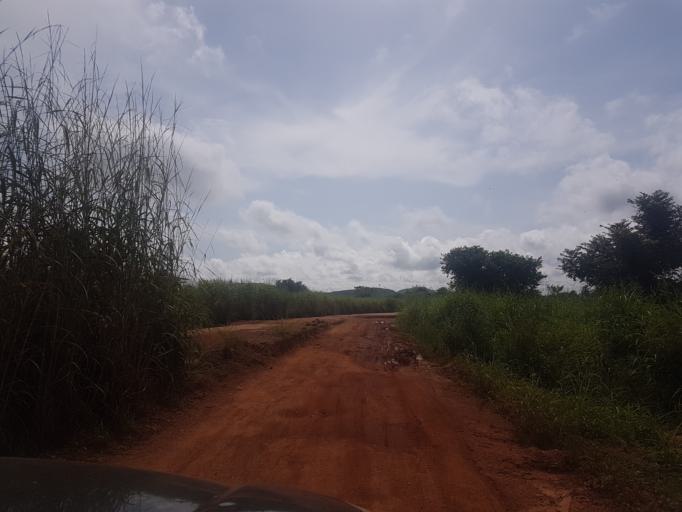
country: GN
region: Nzerekore
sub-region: Prefecture de Guekedou
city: Gueckedou
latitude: 8.6976
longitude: -10.1201
